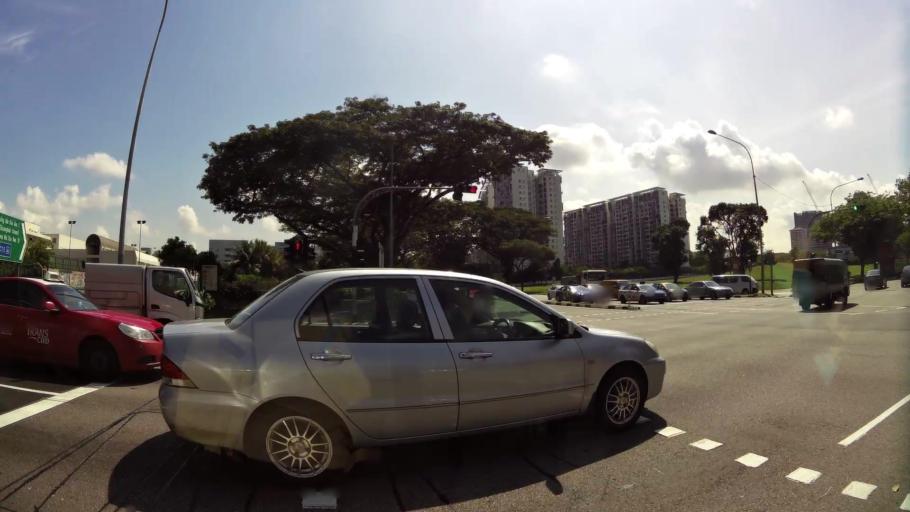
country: SG
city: Singapore
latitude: 1.3774
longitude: 103.8447
